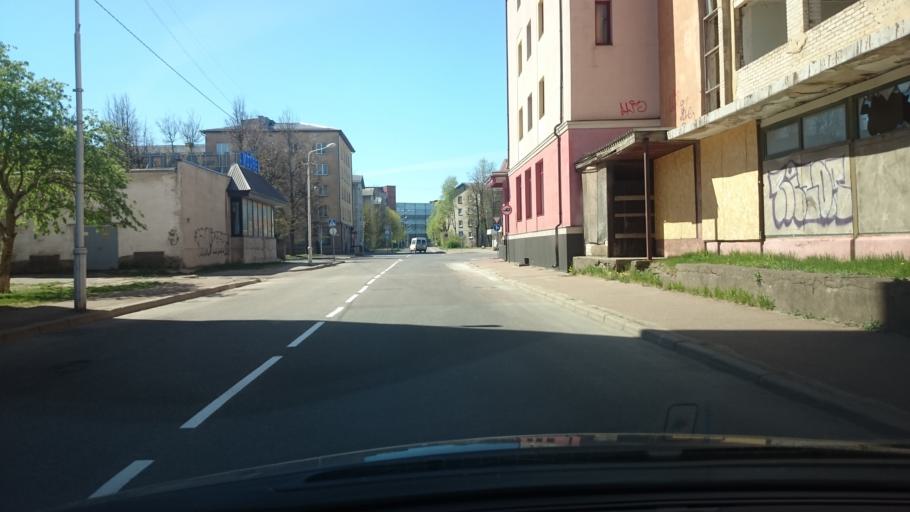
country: EE
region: Ida-Virumaa
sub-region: Narva linn
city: Narva
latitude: 59.3718
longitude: 28.1990
